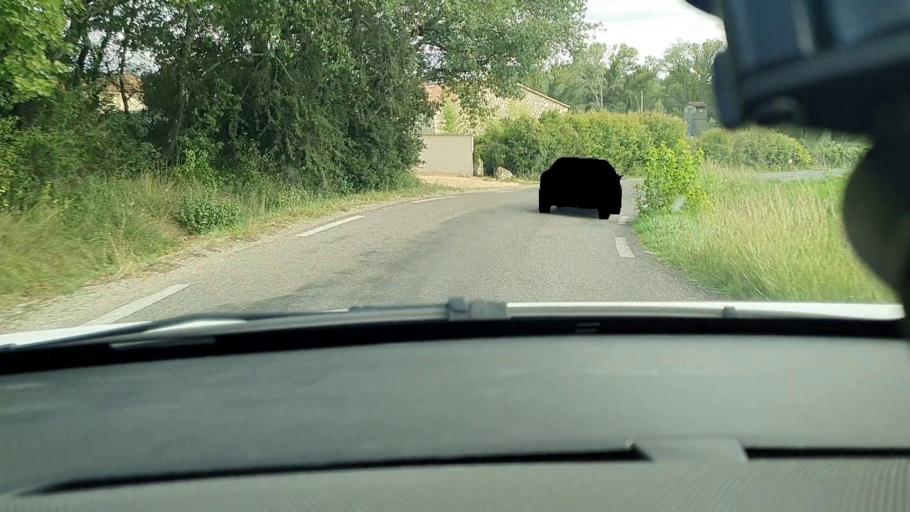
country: FR
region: Languedoc-Roussillon
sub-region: Departement du Gard
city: Les Mages
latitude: 44.2047
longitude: 4.2073
